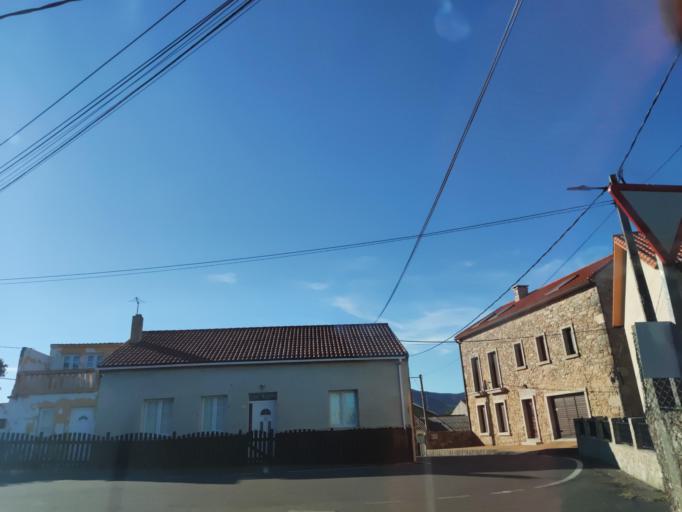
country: ES
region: Galicia
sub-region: Provincia da Coruna
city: Boiro
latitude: 42.5924
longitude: -8.9287
